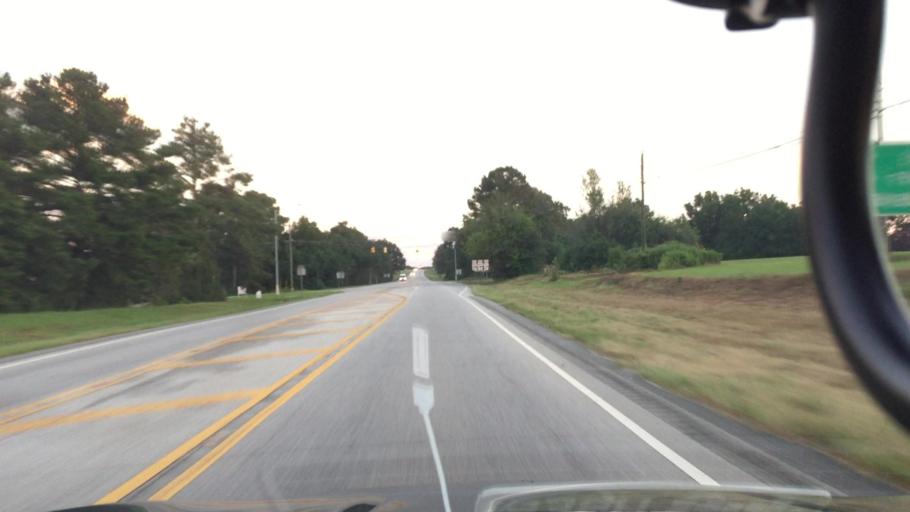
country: US
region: Alabama
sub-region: Coffee County
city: New Brockton
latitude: 31.4284
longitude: -85.8888
